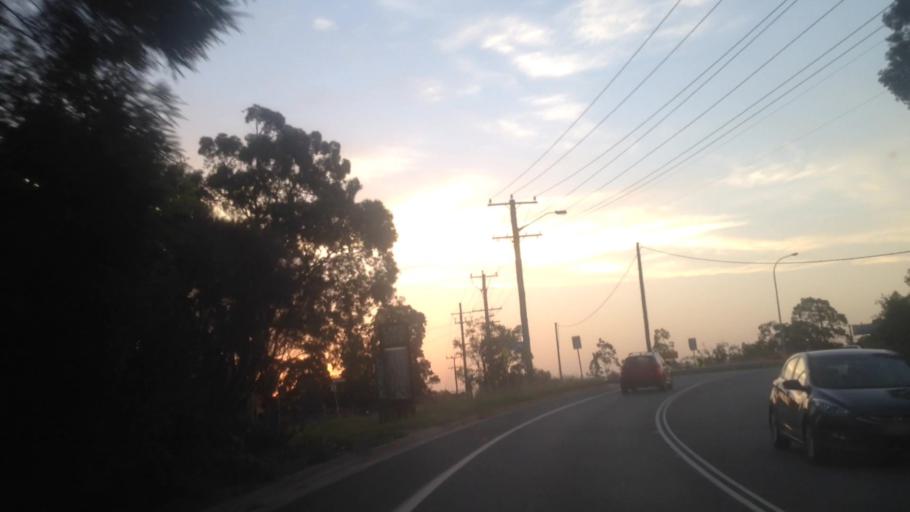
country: AU
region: New South Wales
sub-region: Lake Macquarie Shire
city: Dora Creek
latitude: -33.1075
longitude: 151.4939
